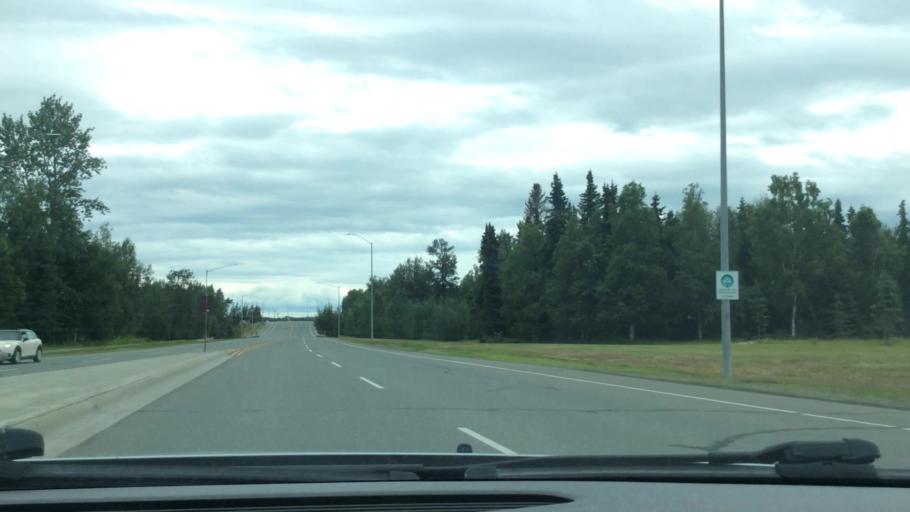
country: US
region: Alaska
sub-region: Anchorage Municipality
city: Anchorage
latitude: 61.2349
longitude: -149.7784
